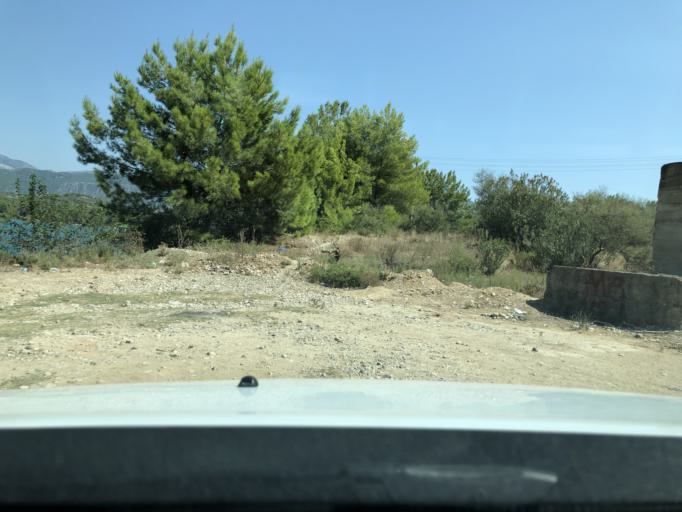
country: TR
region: Antalya
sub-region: Manavgat
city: Manavgat
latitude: 36.8346
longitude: 31.5219
